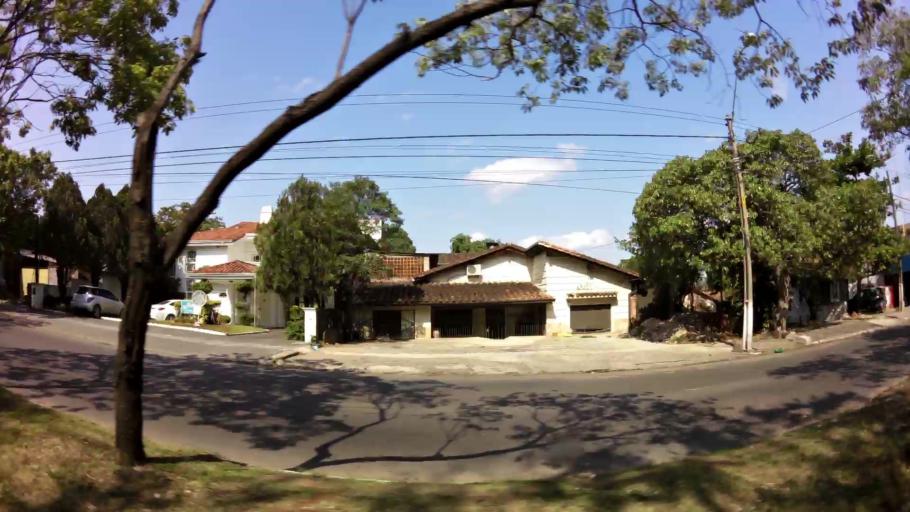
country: PY
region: Asuncion
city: Asuncion
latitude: -25.3058
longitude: -57.6320
